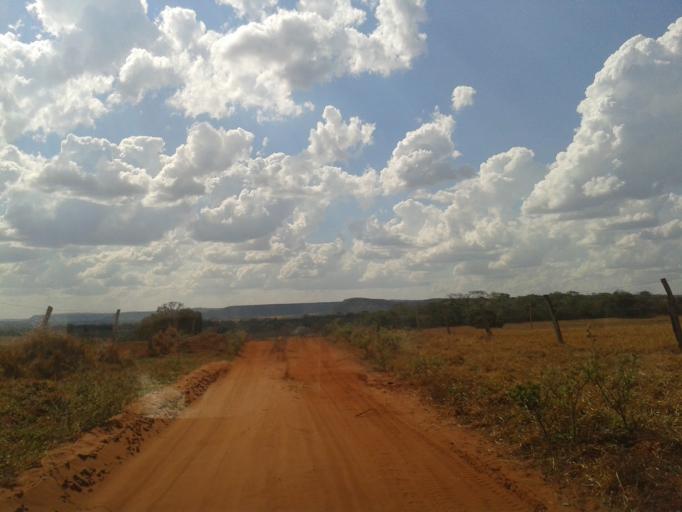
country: BR
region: Minas Gerais
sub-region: Santa Vitoria
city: Santa Vitoria
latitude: -19.2058
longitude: -49.9689
